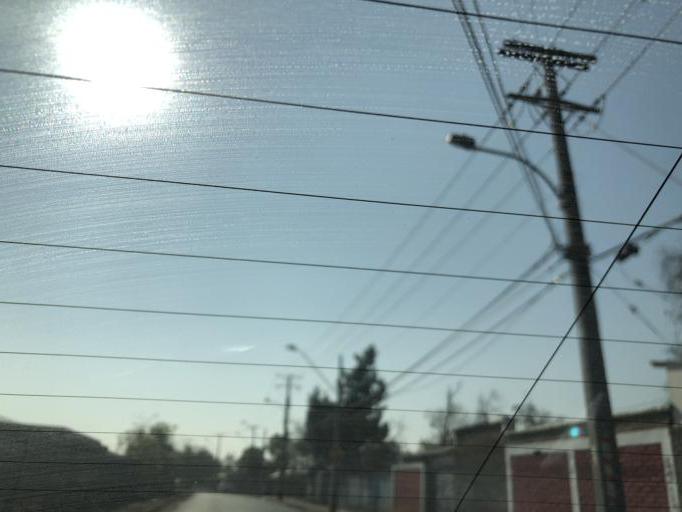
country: CL
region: Santiago Metropolitan
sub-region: Provincia de Cordillera
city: Puente Alto
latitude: -33.6066
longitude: -70.5676
